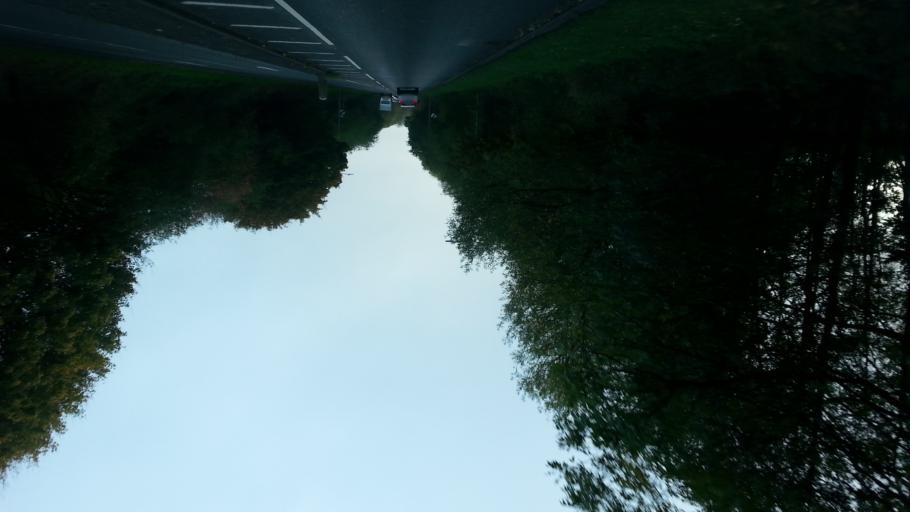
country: GB
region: England
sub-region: Worcestershire
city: Bromsgrove
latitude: 52.3474
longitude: -2.0481
